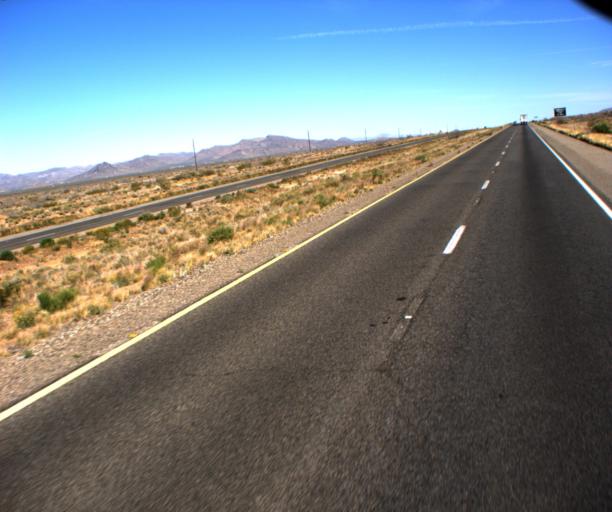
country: US
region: Arizona
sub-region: Mohave County
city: Golden Valley
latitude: 35.2847
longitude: -114.1778
